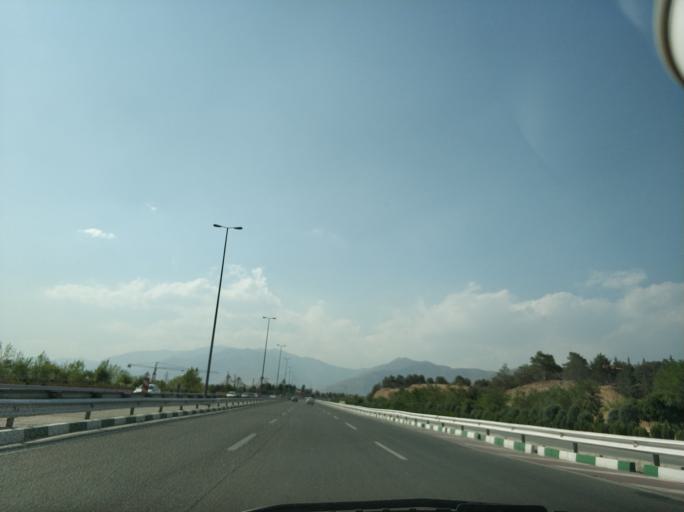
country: IR
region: Tehran
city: Tajrish
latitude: 35.7653
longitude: 51.5376
